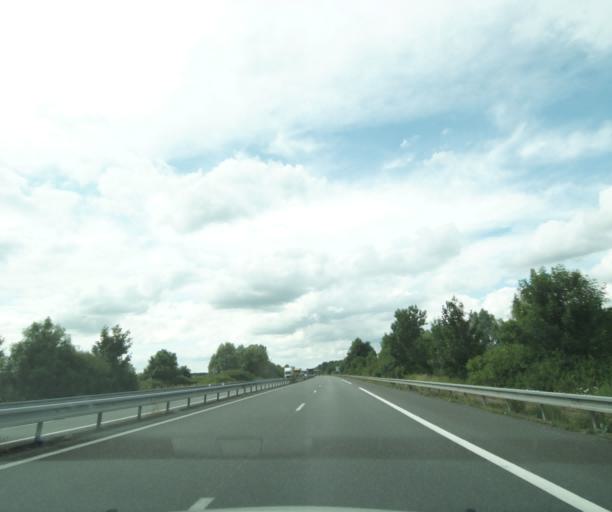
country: FR
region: Centre
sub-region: Departement du Cher
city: Foecy
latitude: 47.1826
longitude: 2.1725
